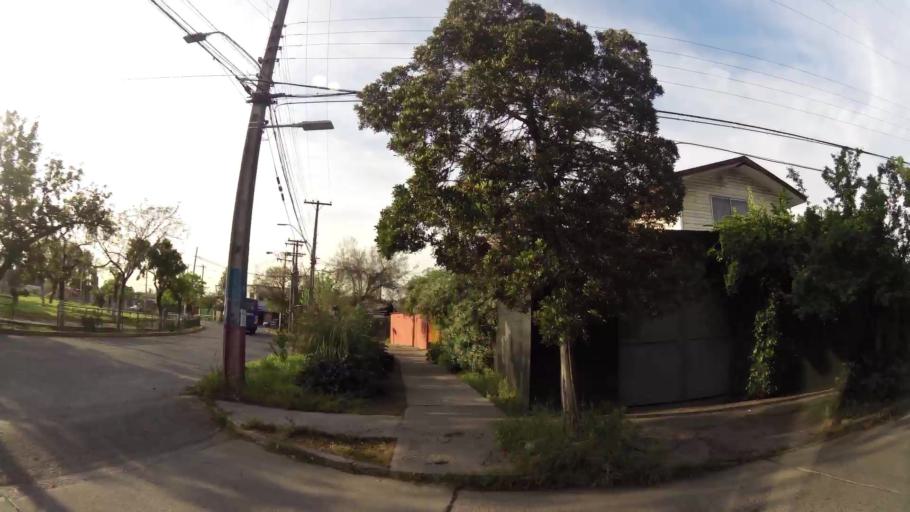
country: CL
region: Santiago Metropolitan
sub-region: Provincia de Santiago
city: La Pintana
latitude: -33.5273
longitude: -70.6730
